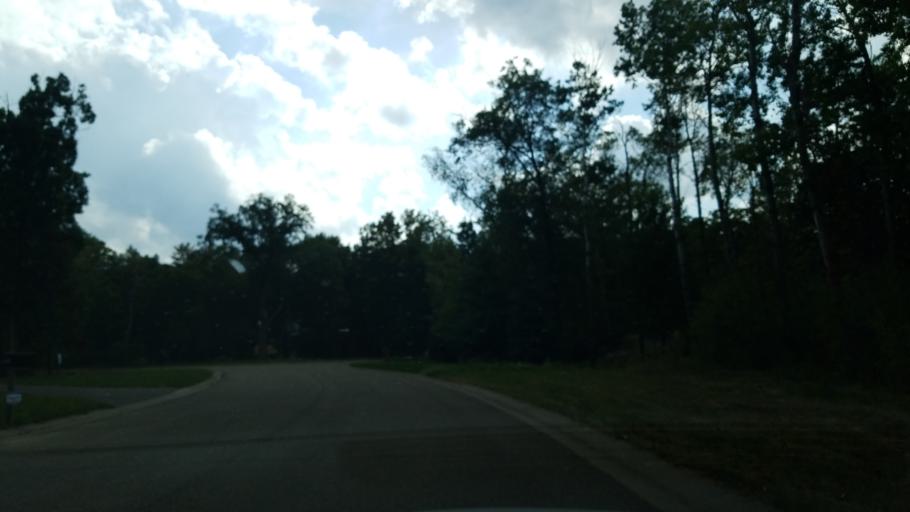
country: US
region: Minnesota
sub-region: Washington County
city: Lake Saint Croix Beach
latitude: 44.9044
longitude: -92.7428
